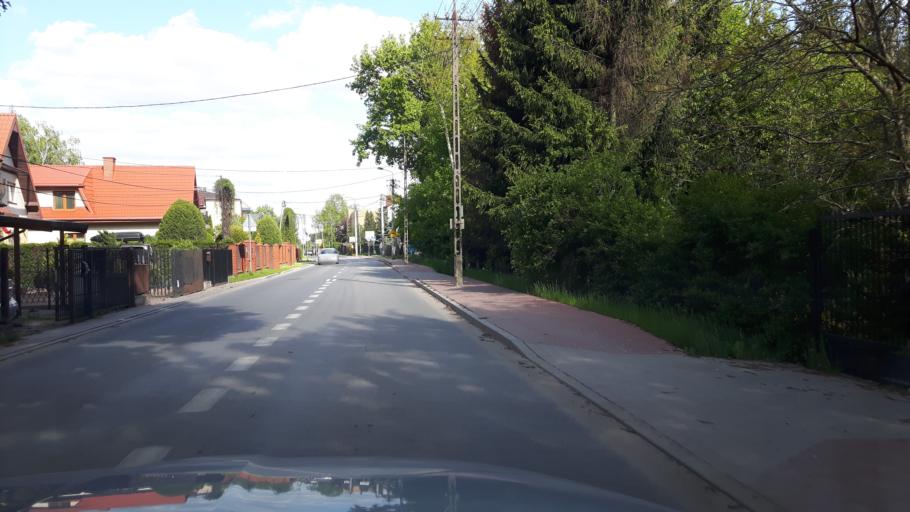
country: PL
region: Masovian Voivodeship
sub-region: Powiat wolominski
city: Marki
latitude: 52.3144
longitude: 21.1313
